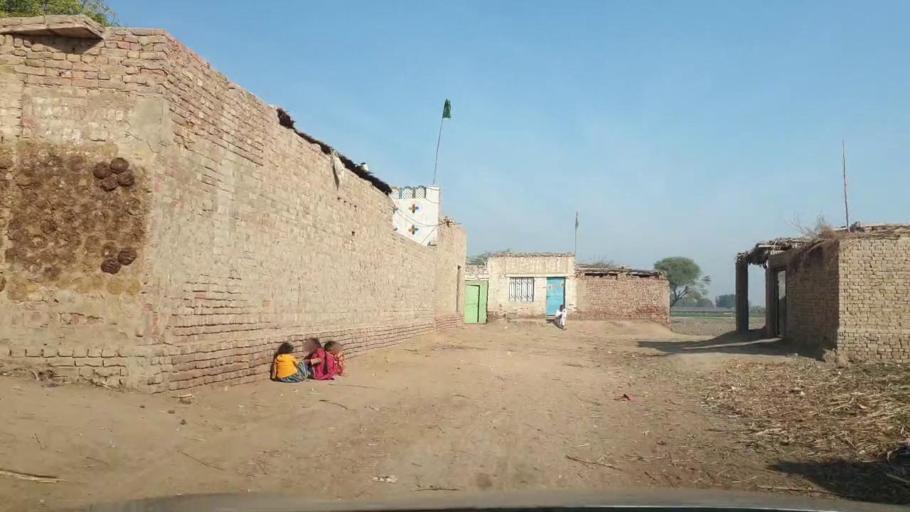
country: PK
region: Sindh
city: Tando Allahyar
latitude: 25.5932
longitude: 68.7233
